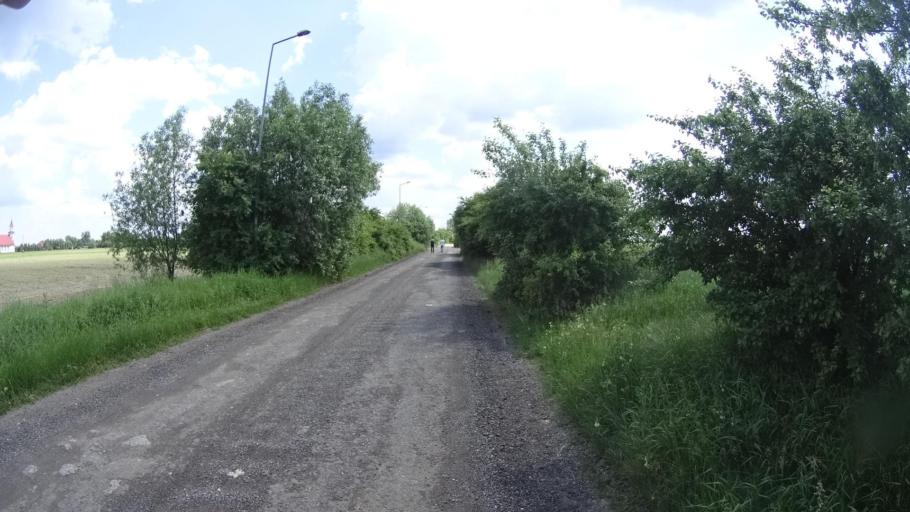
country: PL
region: Masovian Voivodeship
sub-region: Powiat pruszkowski
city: Nadarzyn
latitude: 52.0567
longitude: 20.8239
